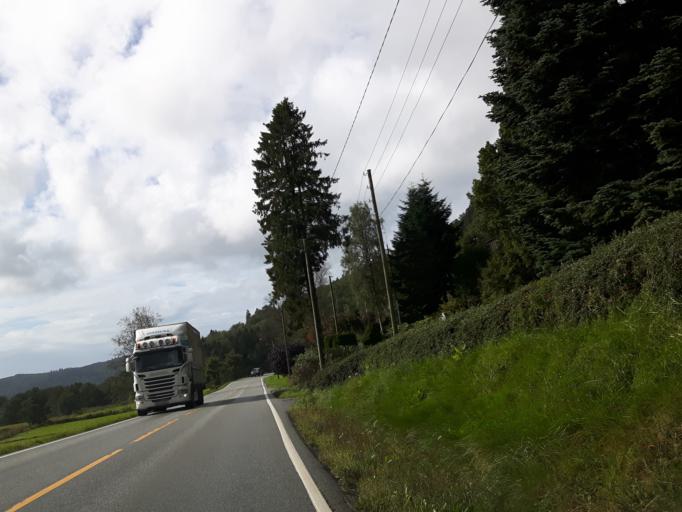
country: NO
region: Vest-Agder
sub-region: Lyngdal
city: Lyngdal
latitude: 58.1532
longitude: 7.0676
